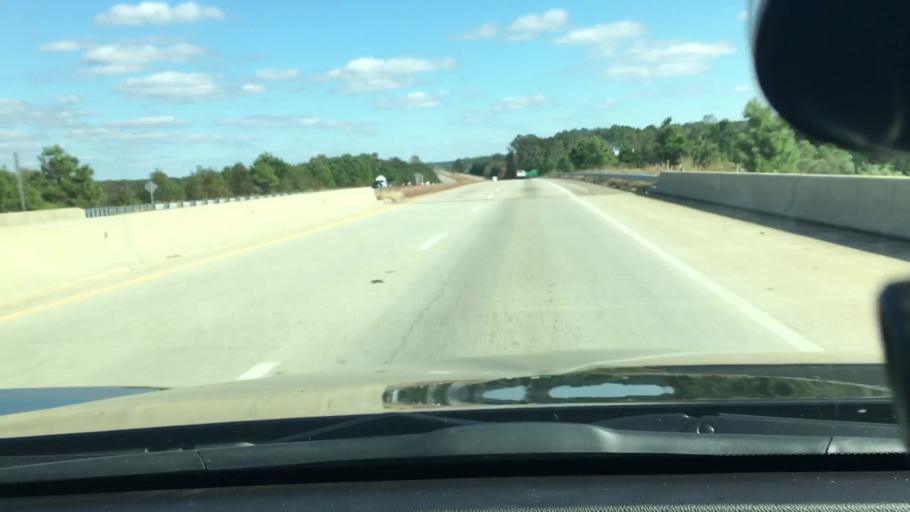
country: US
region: North Carolina
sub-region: Wilson County
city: Wilson
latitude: 35.6753
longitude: -77.9335
